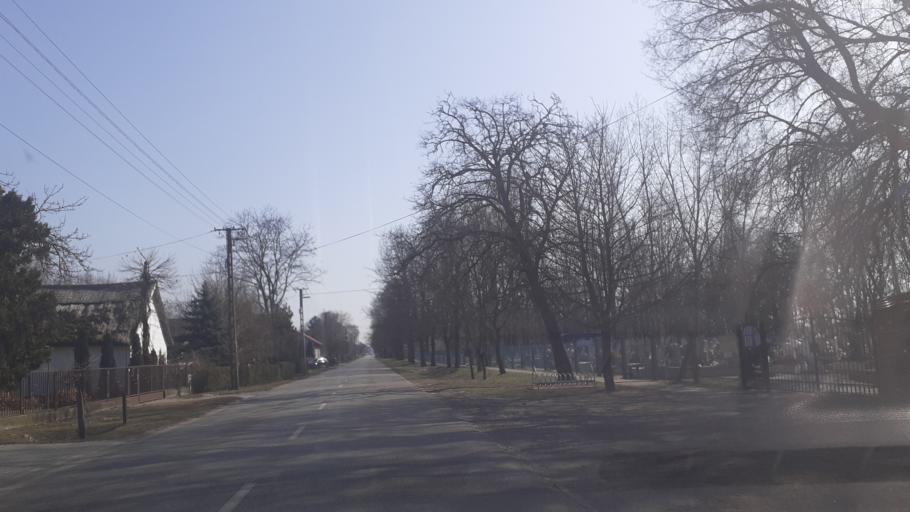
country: HU
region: Pest
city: Taborfalva
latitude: 47.0360
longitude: 19.4494
